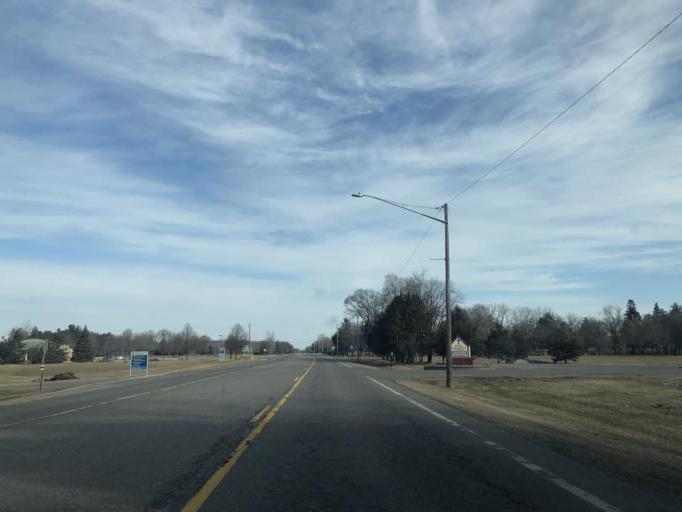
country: US
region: Minnesota
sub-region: Sherburne County
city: Becker
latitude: 45.3994
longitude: -93.8703
